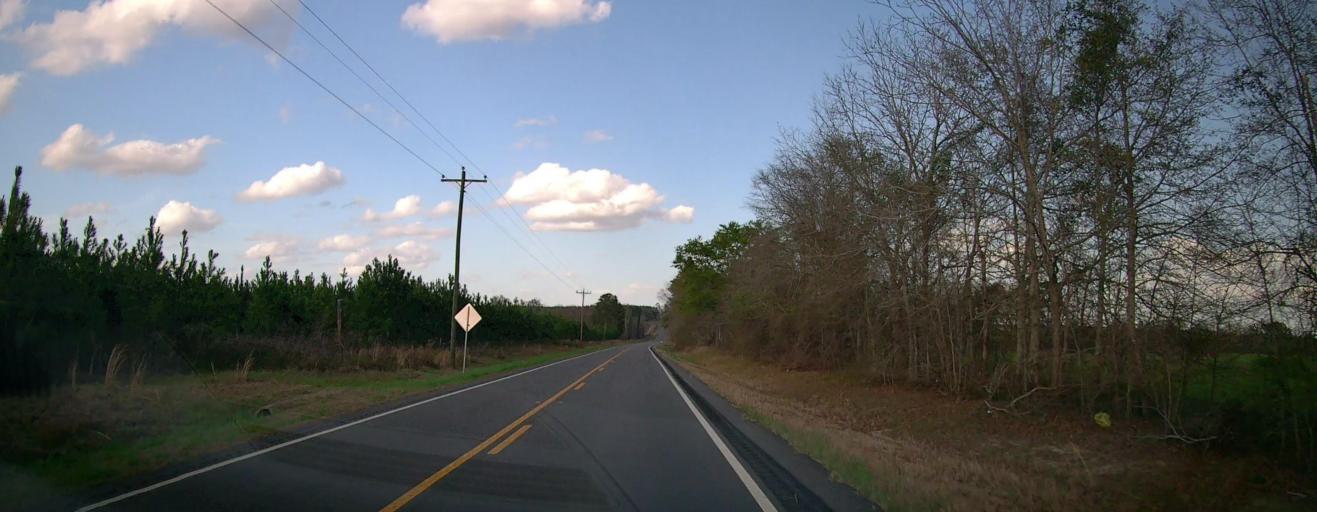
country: US
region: Georgia
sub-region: Wheeler County
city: Alamo
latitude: 32.1030
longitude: -82.8069
